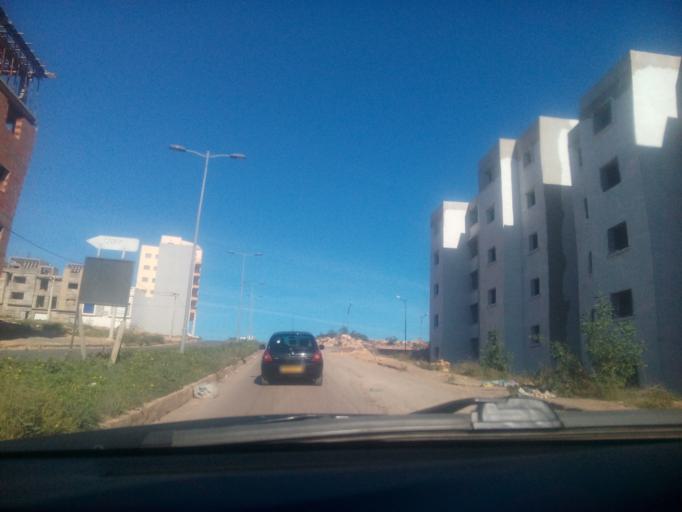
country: DZ
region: Oran
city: Bir el Djir
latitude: 35.7451
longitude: -0.5489
